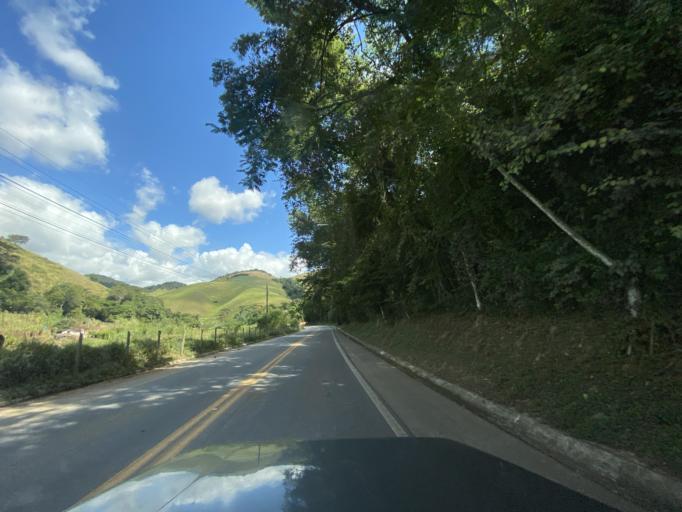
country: BR
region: Espirito Santo
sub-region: Alegre
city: Alegre
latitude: -20.7641
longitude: -41.5076
